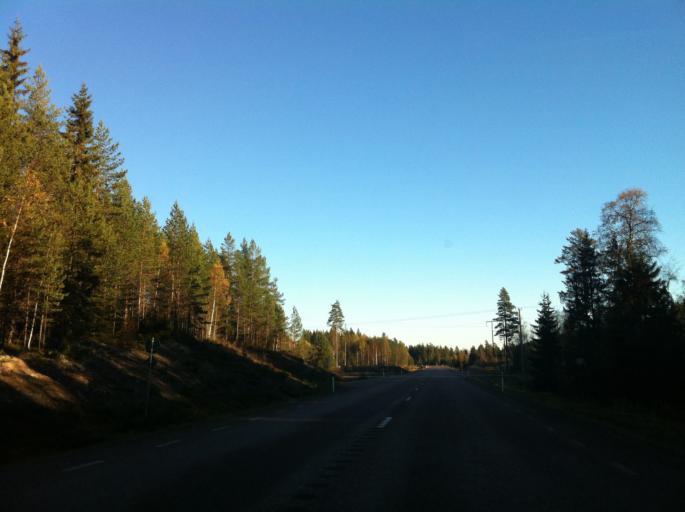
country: SE
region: Dalarna
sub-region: Faluns Kommun
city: Bjursas
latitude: 60.7502
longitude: 15.3526
